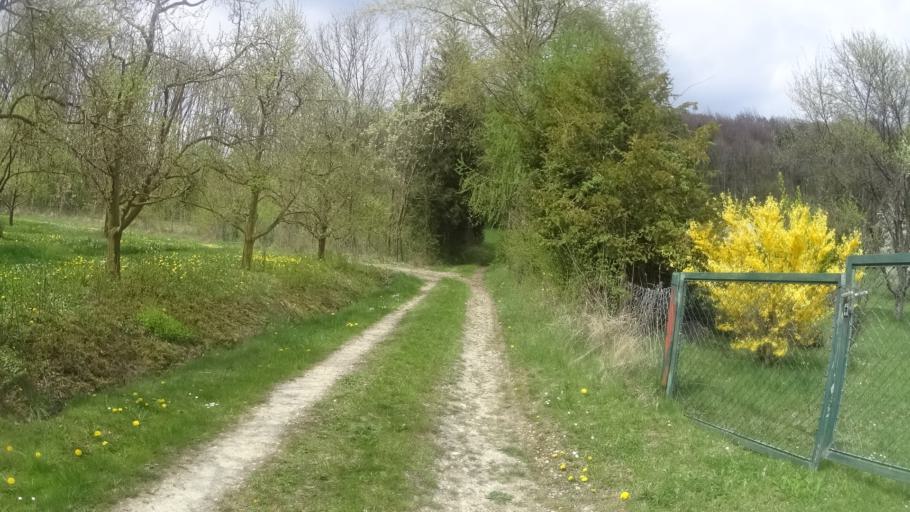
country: DE
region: Bavaria
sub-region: Upper Franconia
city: Kleinsendelbach
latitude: 49.6239
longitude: 11.1832
